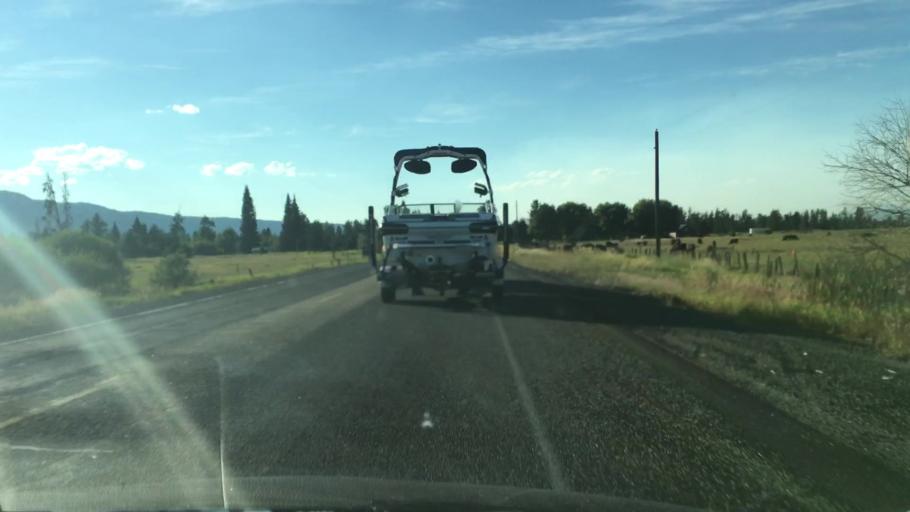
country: US
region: Idaho
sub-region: Valley County
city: McCall
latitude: 44.7221
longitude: -116.0689
